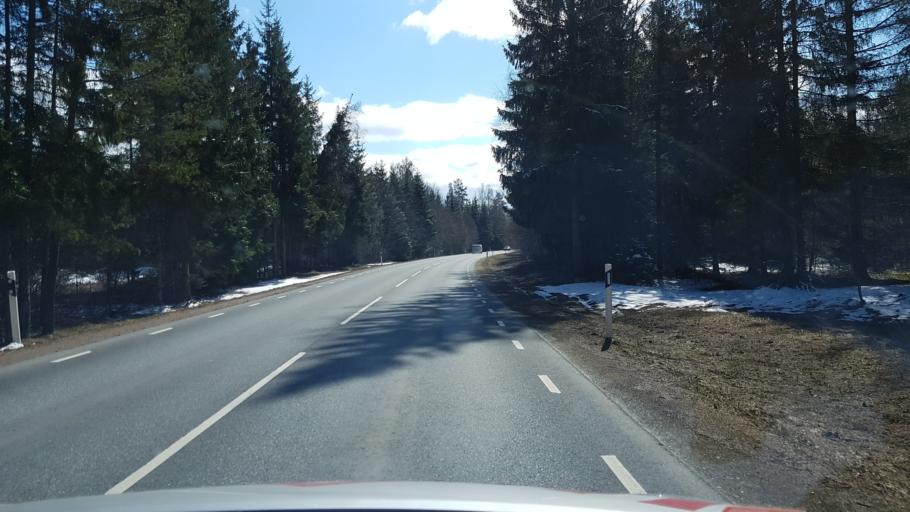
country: EE
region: Laeaene-Virumaa
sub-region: Kadrina vald
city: Kadrina
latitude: 59.3898
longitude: 26.0161
